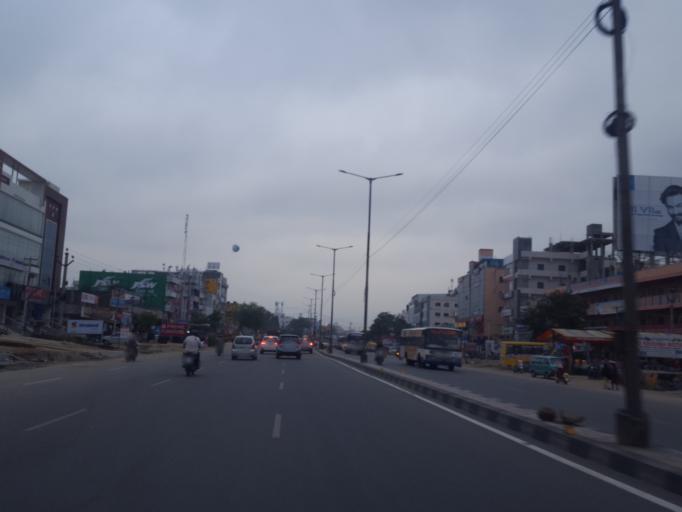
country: IN
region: Telangana
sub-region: Medak
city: Serilingampalle
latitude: 17.5102
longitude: 78.2977
